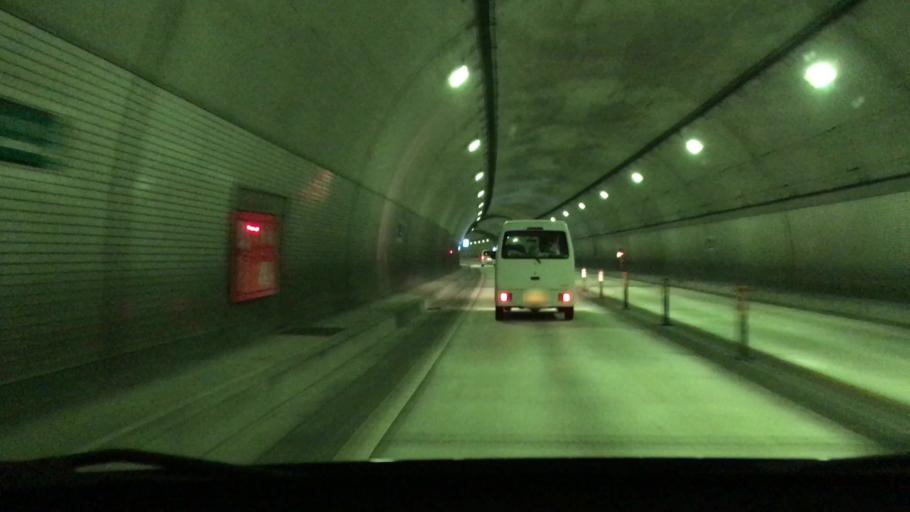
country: JP
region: Nagasaki
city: Sasebo
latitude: 33.0961
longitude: 129.7790
